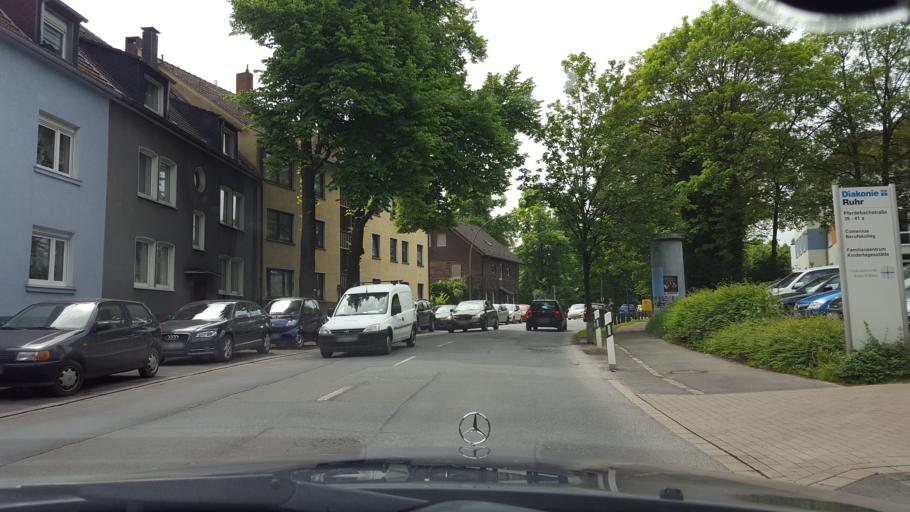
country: DE
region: North Rhine-Westphalia
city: Witten
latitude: 51.4467
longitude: 7.3470
